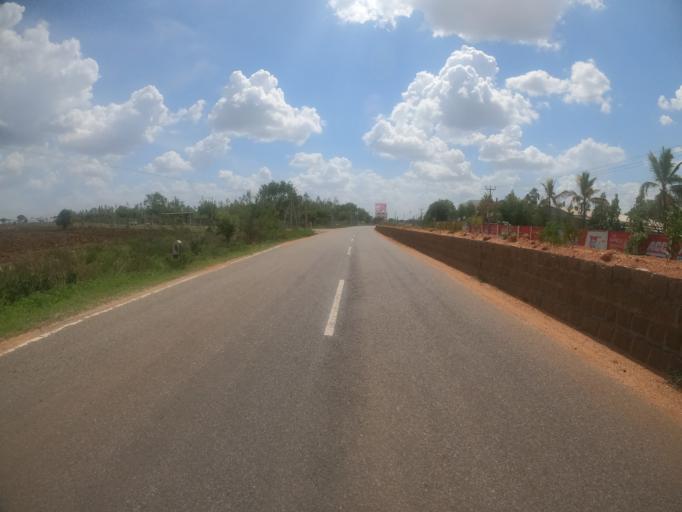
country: IN
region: Telangana
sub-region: Rangareddi
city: Sriramnagar
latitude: 17.3049
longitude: 78.1497
